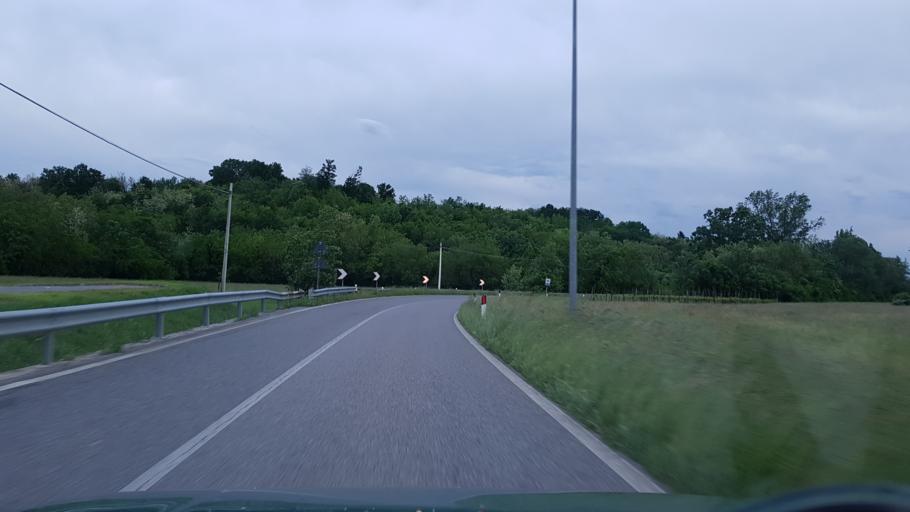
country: IT
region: Friuli Venezia Giulia
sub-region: Provincia di Udine
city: Faedis
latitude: 46.1397
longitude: 13.3498
